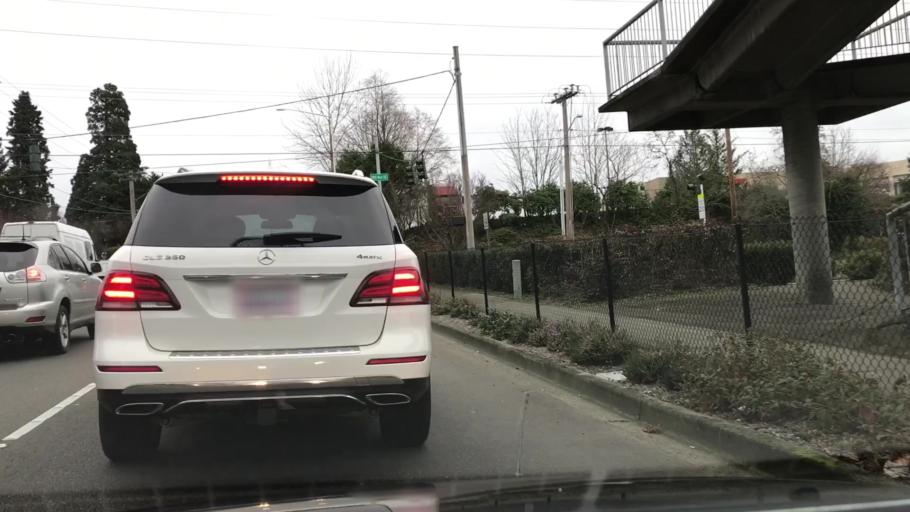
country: US
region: Washington
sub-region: King County
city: Kent
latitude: 47.3869
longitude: -122.2081
